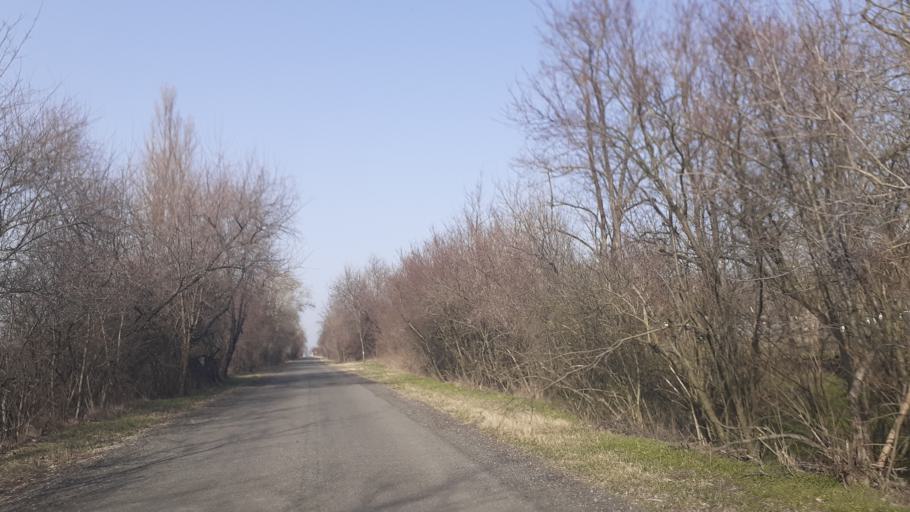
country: HU
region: Pest
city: Dabas
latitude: 47.1108
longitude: 19.2216
